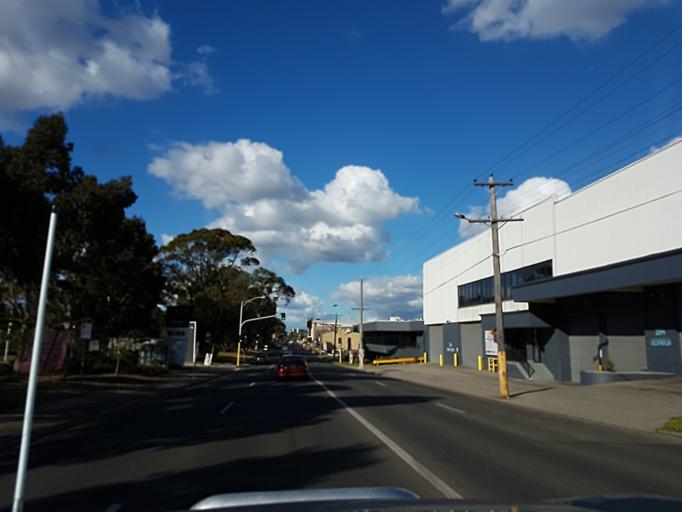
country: AU
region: Victoria
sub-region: Darebin
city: Fairfield
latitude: -37.7657
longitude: 145.0231
